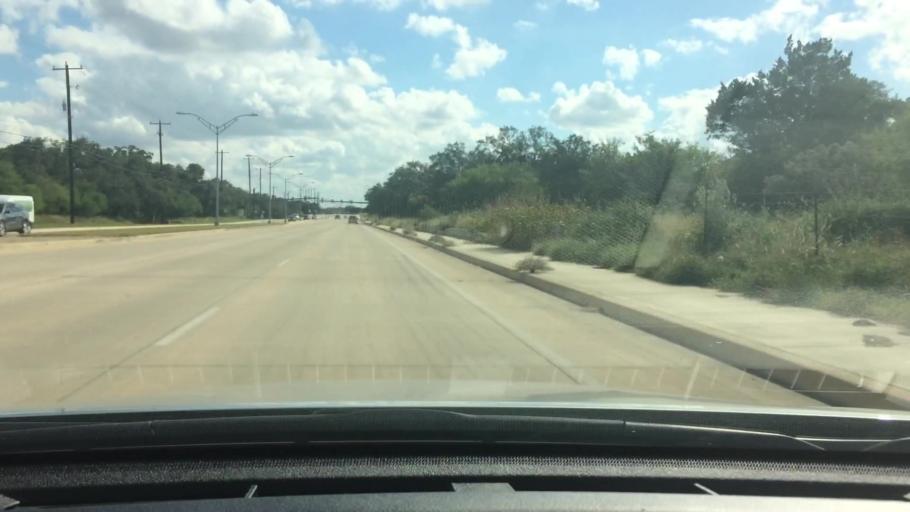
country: US
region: Texas
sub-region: Bexar County
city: Hollywood Park
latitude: 29.6254
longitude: -98.4239
